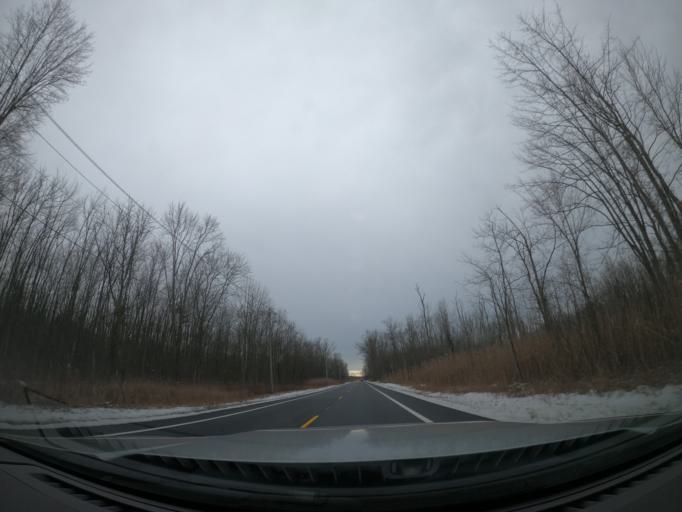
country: US
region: New York
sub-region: Madison County
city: Bridgeport
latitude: 43.1365
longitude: -75.9845
